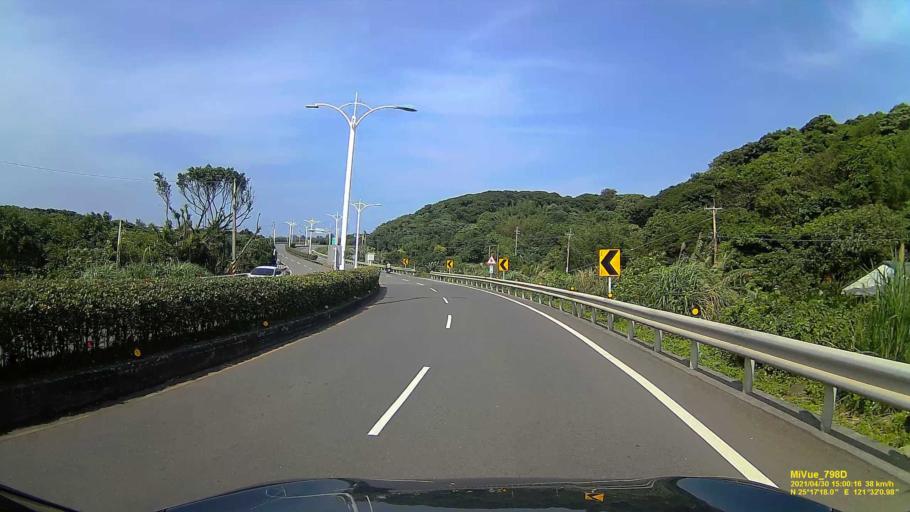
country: TW
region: Taipei
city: Taipei
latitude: 25.2885
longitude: 121.5338
